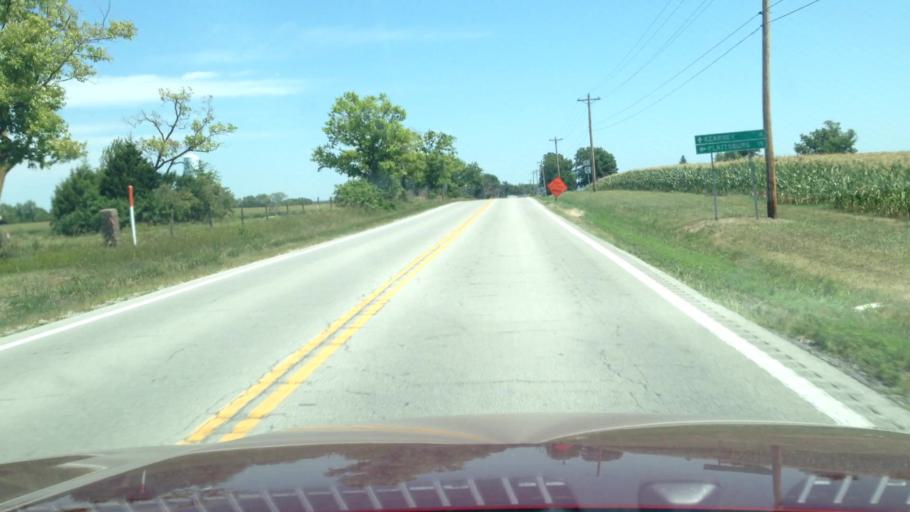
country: US
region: Missouri
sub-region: Clay County
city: Kearney
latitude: 39.3678
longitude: -94.4479
